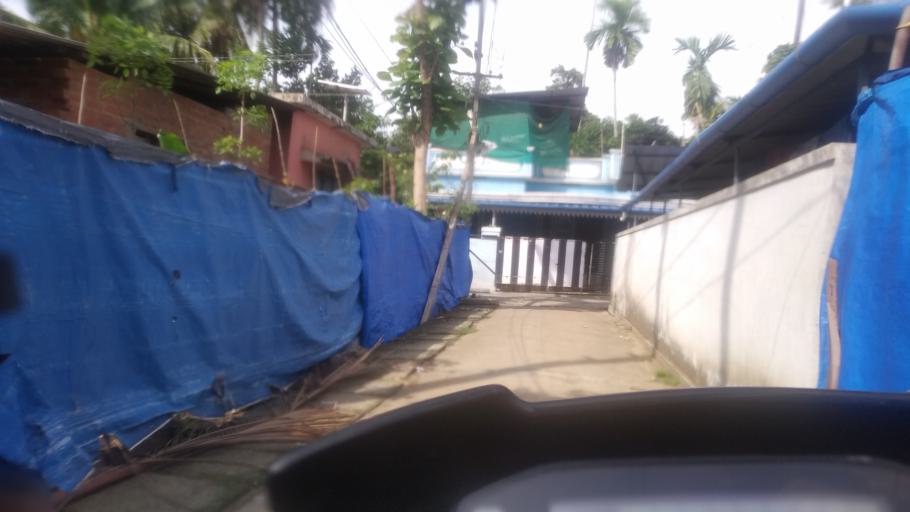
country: IN
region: Kerala
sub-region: Ernakulam
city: Elur
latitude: 10.0712
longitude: 76.2097
